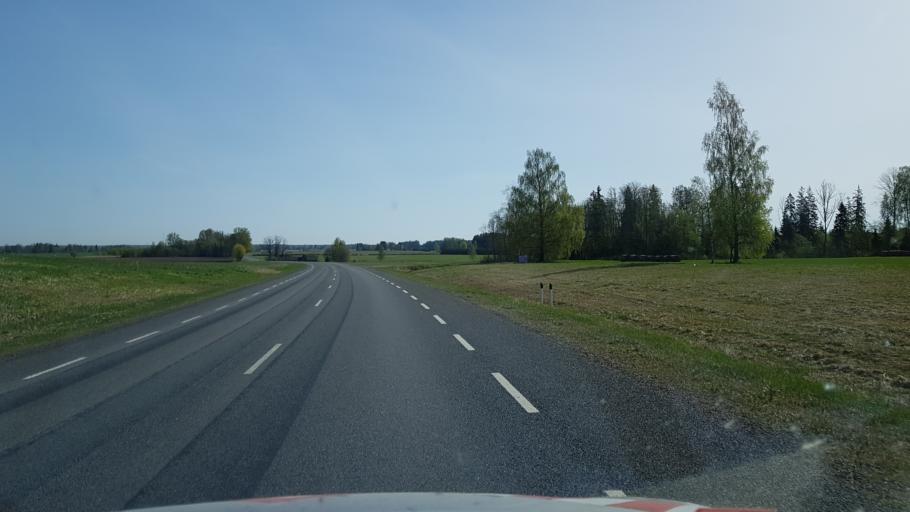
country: EE
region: Viljandimaa
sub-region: Karksi vald
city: Karksi-Nuia
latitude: 58.1672
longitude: 25.4655
